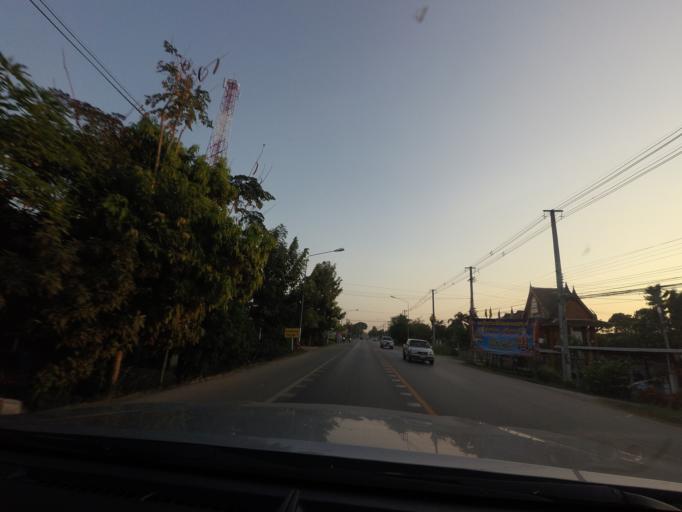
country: TH
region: Sukhothai
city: Si Samrong
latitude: 17.1217
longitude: 99.8509
